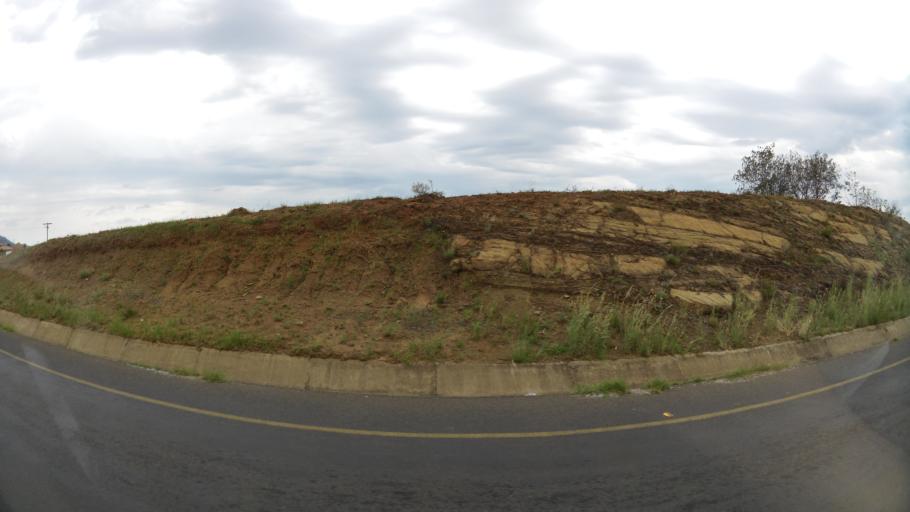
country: LS
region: Maseru
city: Maseru
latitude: -29.3993
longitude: 27.4734
